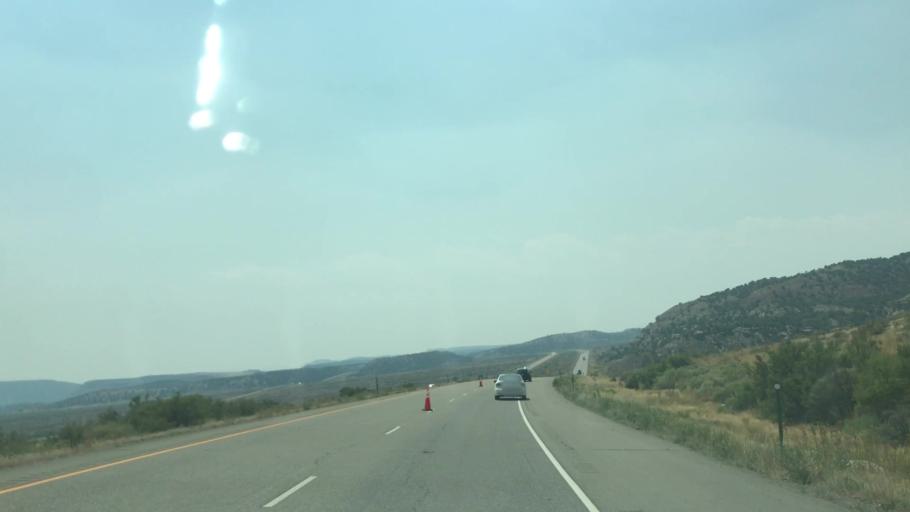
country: US
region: Colorado
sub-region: Garfield County
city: Parachute
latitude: 39.3912
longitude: -108.1315
